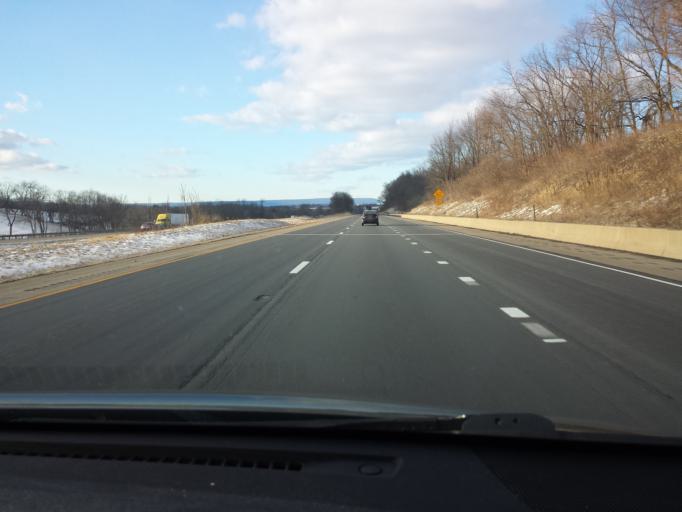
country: US
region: Pennsylvania
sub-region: Northumberland County
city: Milton
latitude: 41.0269
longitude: -76.8021
